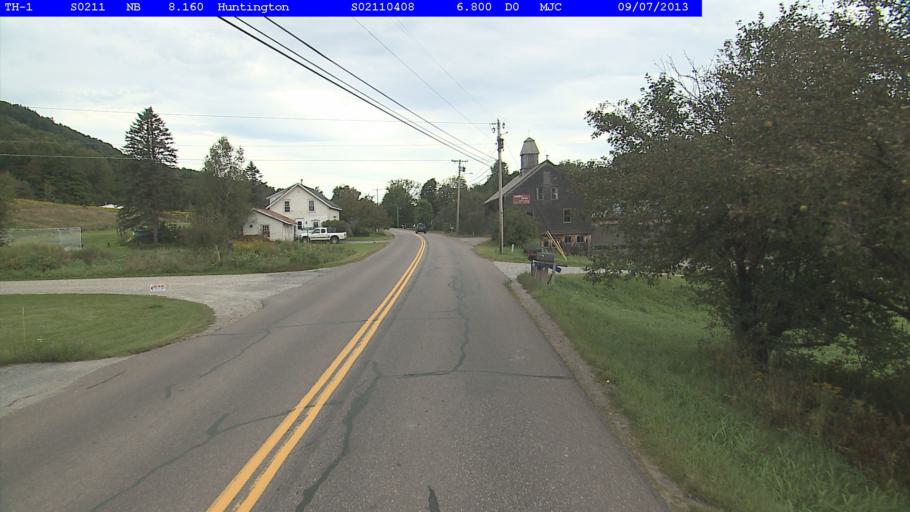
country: US
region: Vermont
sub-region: Chittenden County
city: Hinesburg
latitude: 44.3168
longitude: -72.9891
